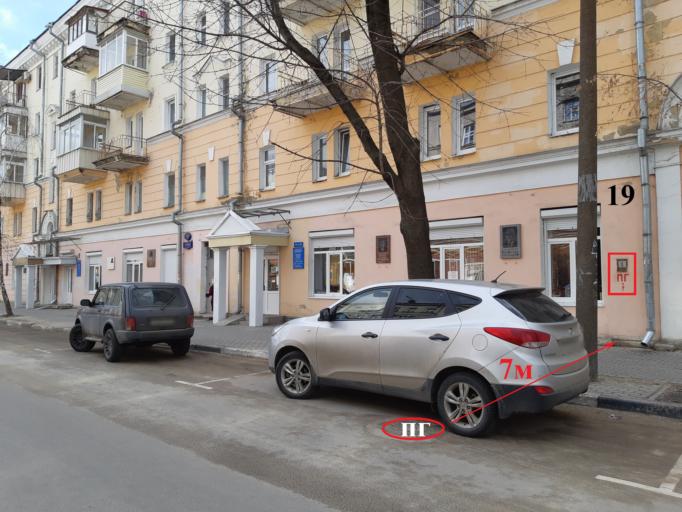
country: RU
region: Voronezj
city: Voronezh
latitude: 51.6649
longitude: 39.2077
